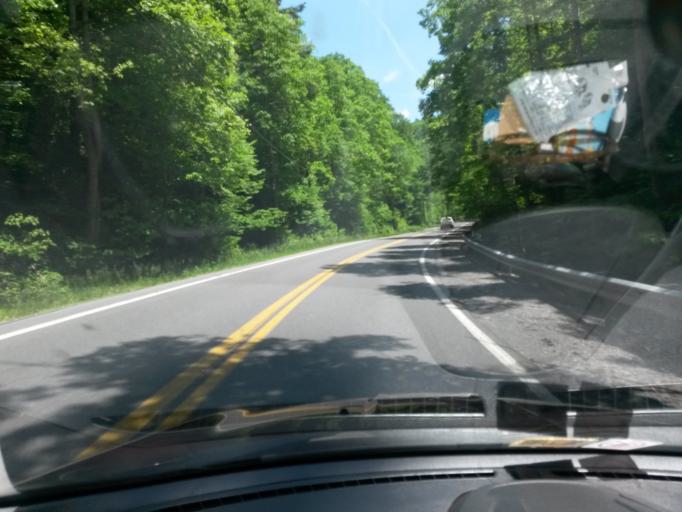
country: US
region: West Virginia
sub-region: Wyoming County
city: Pineville
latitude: 37.5628
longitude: -81.5347
